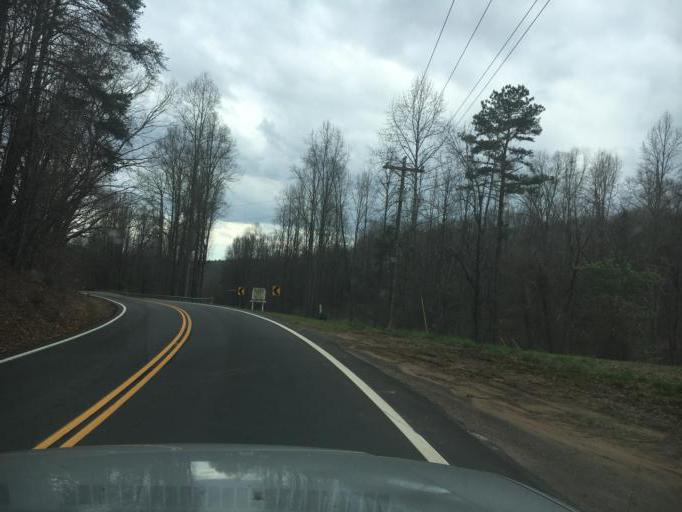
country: US
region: South Carolina
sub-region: Pickens County
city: Pickens
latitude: 34.9822
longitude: -82.7547
